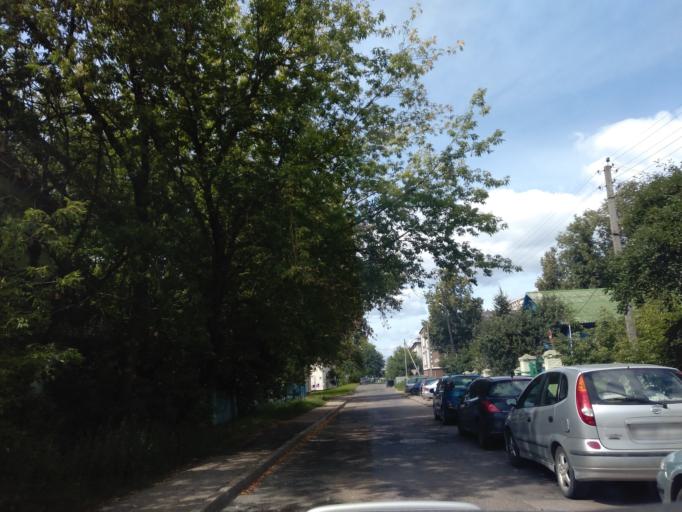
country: BY
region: Minsk
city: Syenitsa
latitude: 53.8793
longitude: 27.5095
